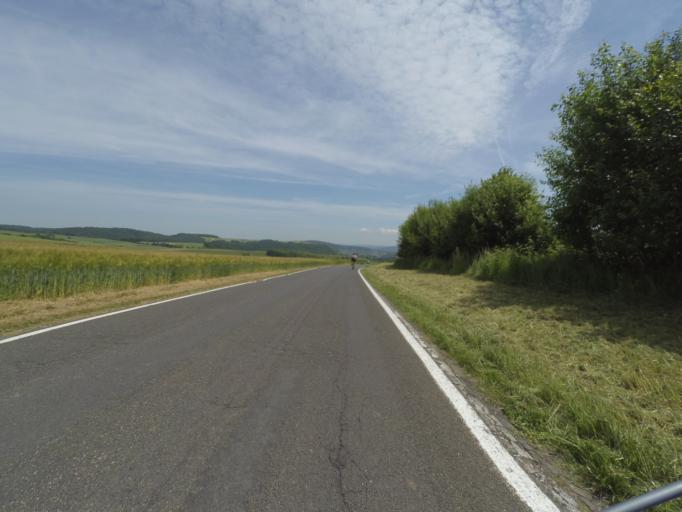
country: DE
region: Rheinland-Pfalz
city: Lonnig
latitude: 50.3110
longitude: 7.4262
